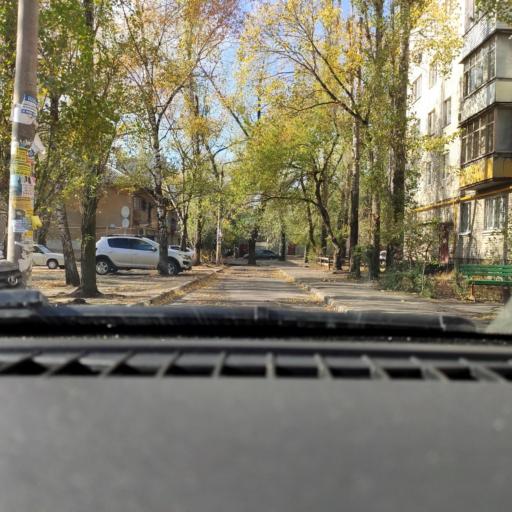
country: RU
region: Voronezj
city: Maslovka
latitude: 51.6352
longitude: 39.2663
